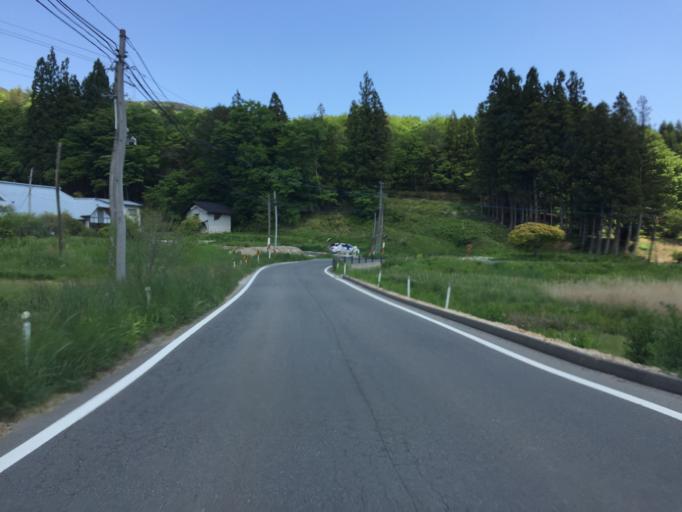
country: JP
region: Fukushima
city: Funehikimachi-funehiki
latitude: 37.5100
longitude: 140.7162
